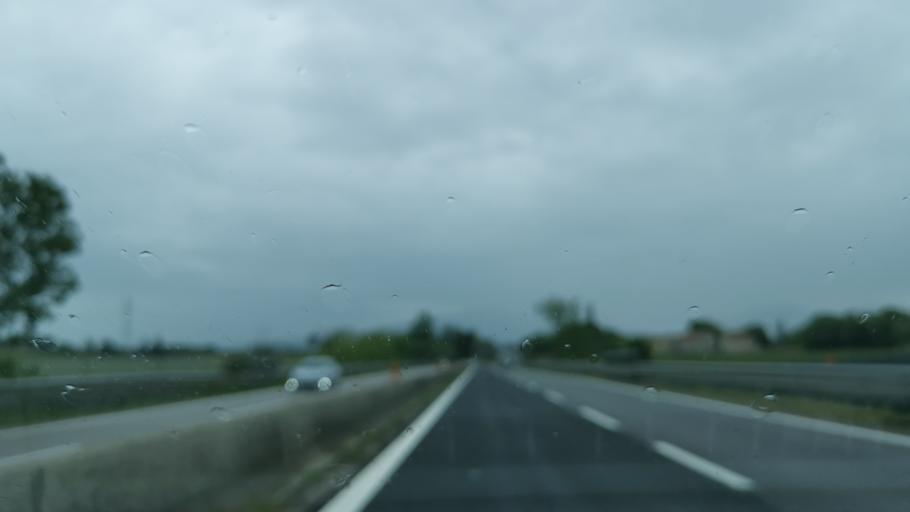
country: IT
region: Veneto
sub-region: Provincia di Verona
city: Cola
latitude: 45.4693
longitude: 10.7611
